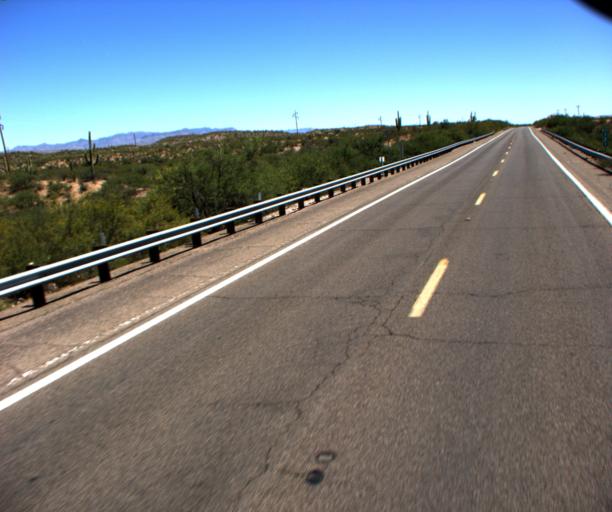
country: US
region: Arizona
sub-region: Pinal County
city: Mammoth
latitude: 32.8100
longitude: -110.6851
